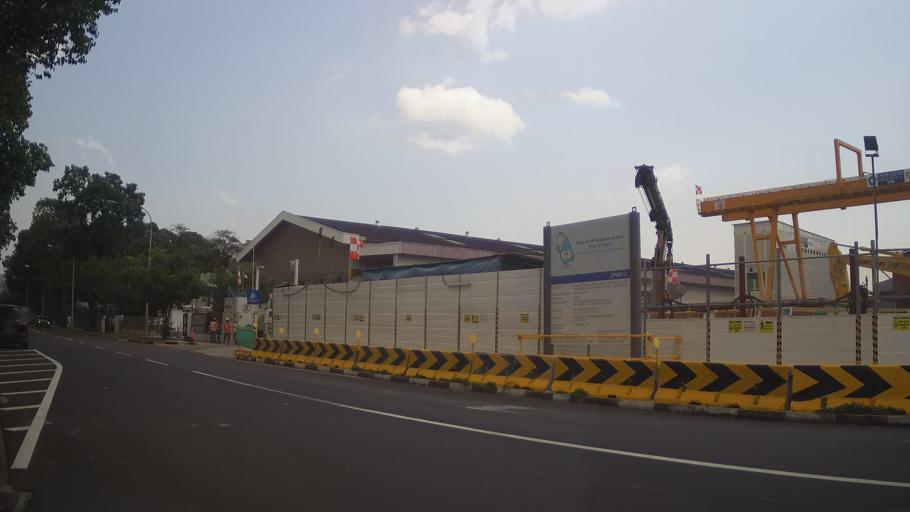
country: MY
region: Johor
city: Johor Bahru
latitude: 1.3087
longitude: 103.6594
